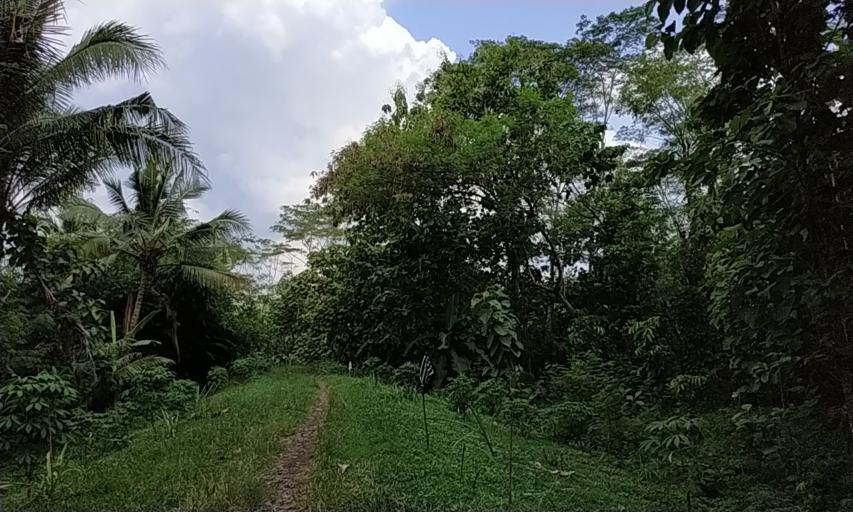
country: ID
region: Central Java
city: Bakung
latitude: -7.3503
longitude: 108.6602
